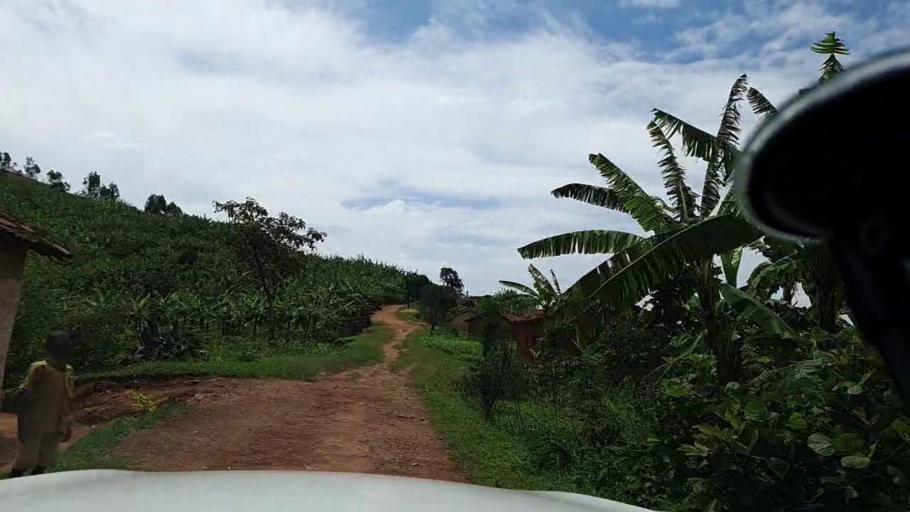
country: RW
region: Southern Province
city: Gitarama
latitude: -2.0796
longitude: 29.6663
